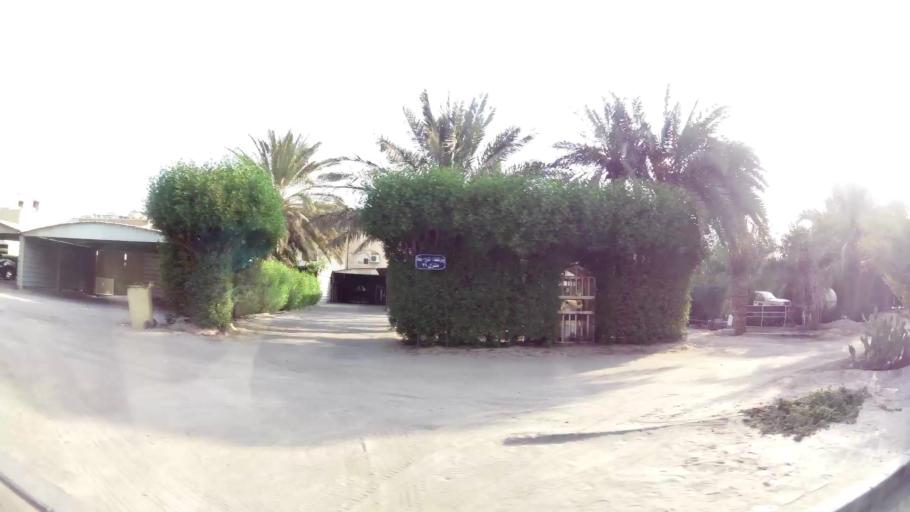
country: KW
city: Bayan
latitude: 29.2886
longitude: 48.0574
